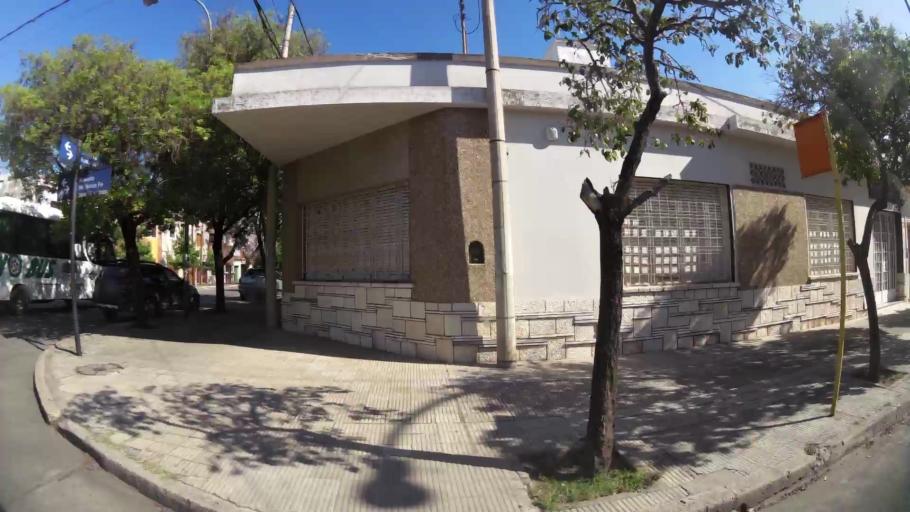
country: AR
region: Cordoba
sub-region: Departamento de Capital
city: Cordoba
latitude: -31.4134
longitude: -64.1565
